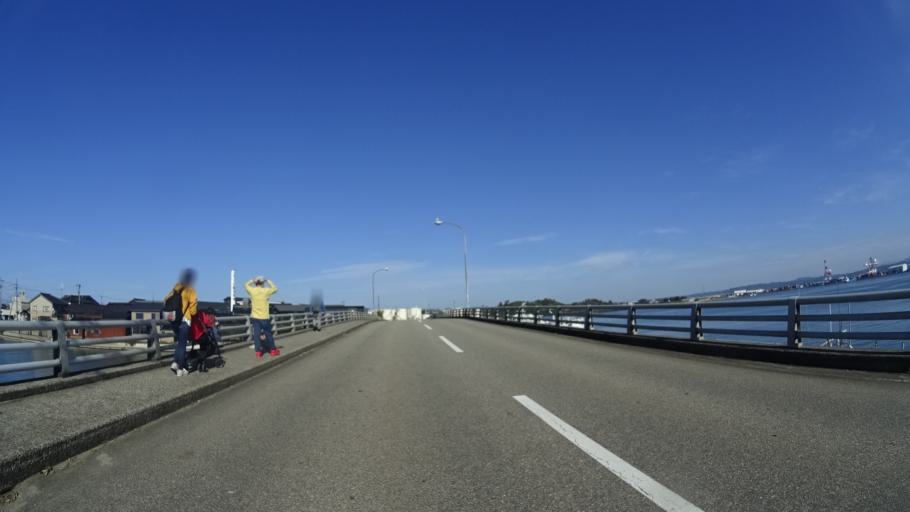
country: JP
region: Ishikawa
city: Kanazawa-shi
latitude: 36.6124
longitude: 136.6075
